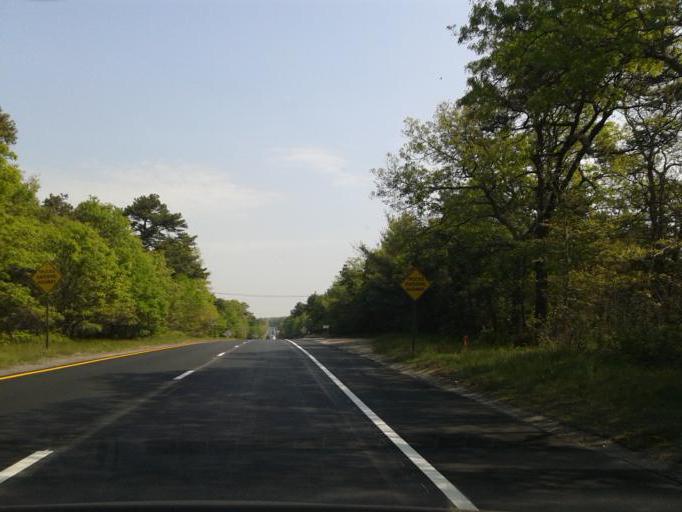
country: US
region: Massachusetts
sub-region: Barnstable County
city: Pocasset
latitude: 41.6885
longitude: -70.5901
